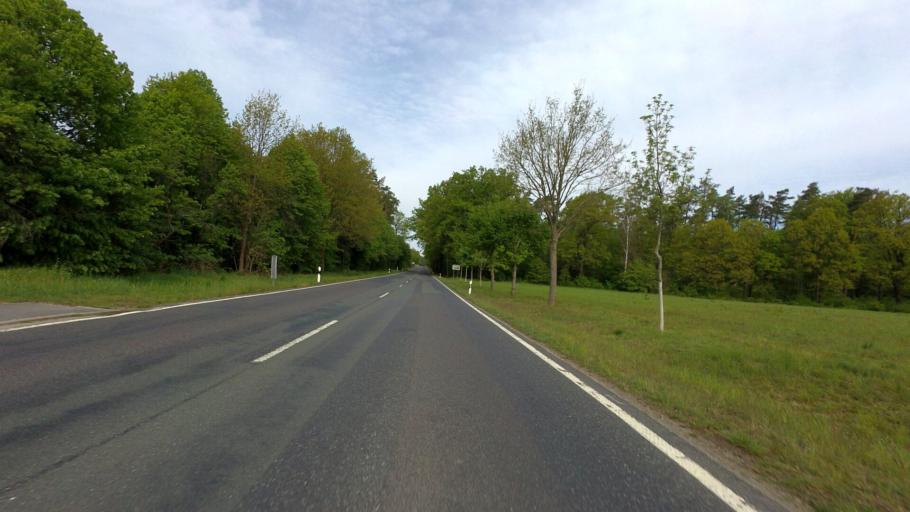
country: DE
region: Saxony
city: Laussnitz
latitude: 51.2611
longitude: 13.8627
